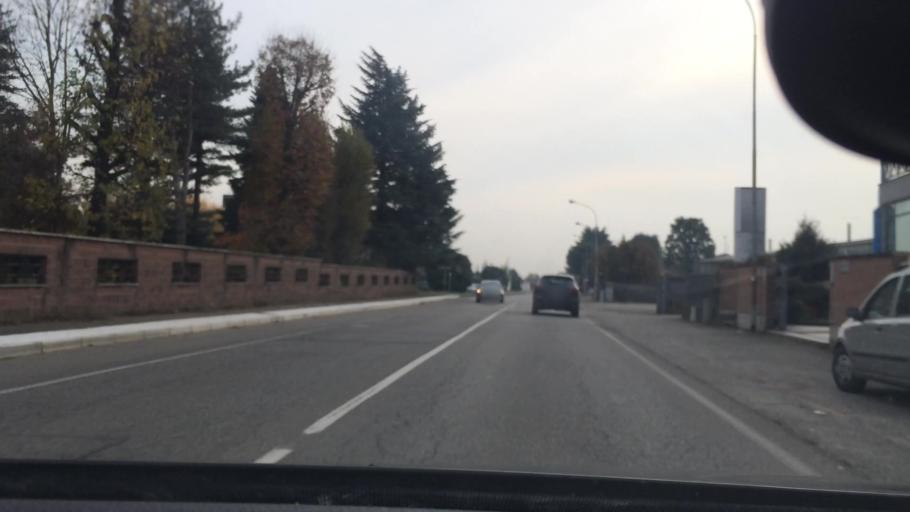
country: IT
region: Lombardy
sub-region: Provincia di Monza e Brianza
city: Misinto
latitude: 45.6632
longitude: 9.0737
